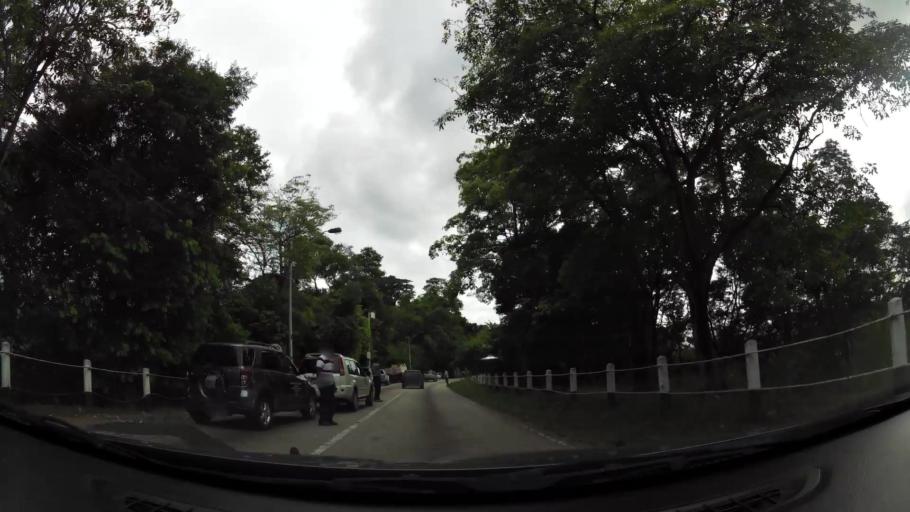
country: TT
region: City of Port of Spain
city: Port-of-Spain
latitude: 10.6743
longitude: -61.5028
